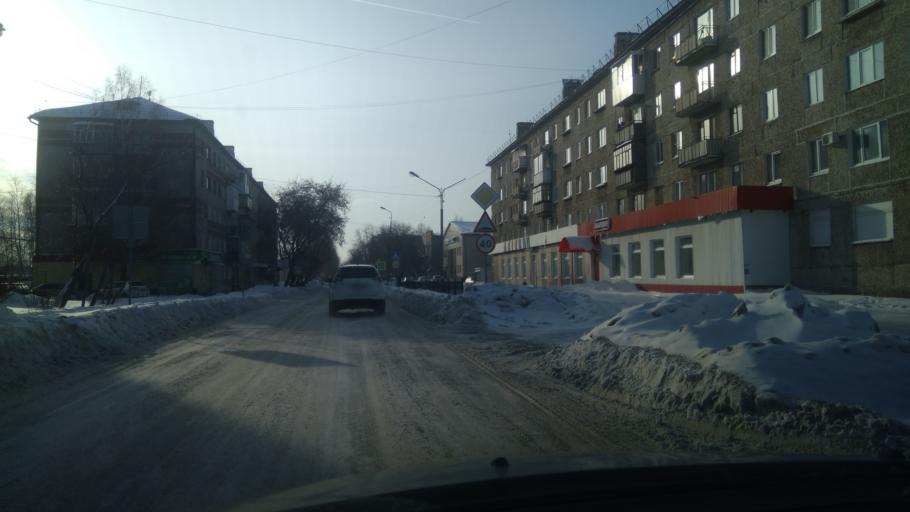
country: RU
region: Sverdlovsk
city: Sukhoy Log
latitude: 56.9040
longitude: 62.0318
